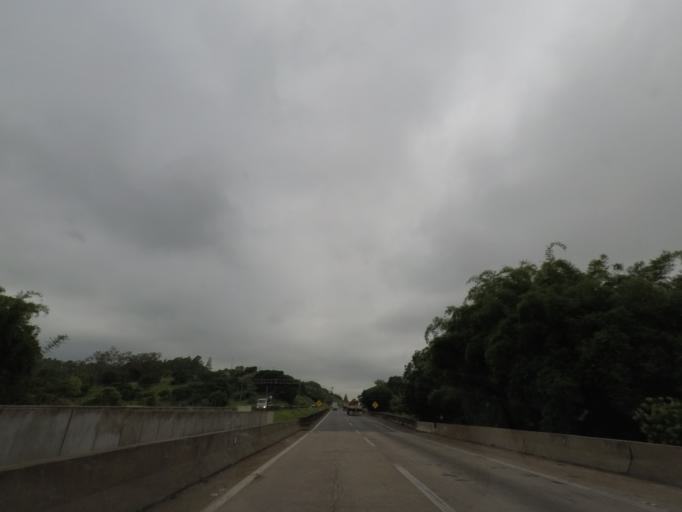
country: BR
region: Sao Paulo
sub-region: Itatiba
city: Itatiba
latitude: -22.9601
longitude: -46.8500
